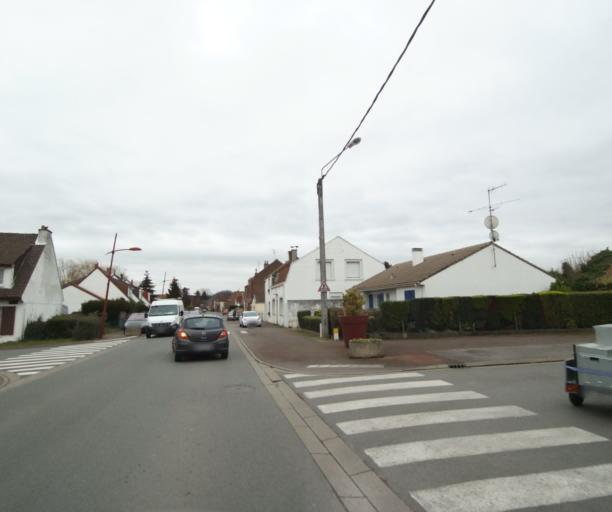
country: FR
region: Nord-Pas-de-Calais
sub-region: Departement du Nord
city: Beuvrages
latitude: 50.3873
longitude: 3.4969
